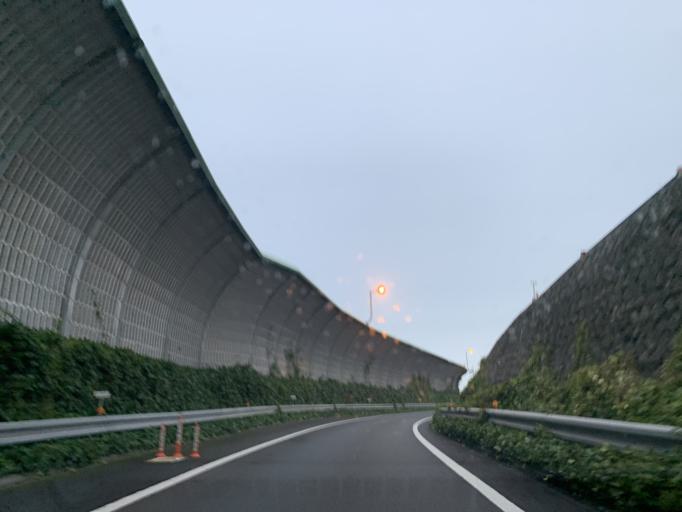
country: JP
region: Chiba
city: Funabashi
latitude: 35.6688
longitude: 140.0356
